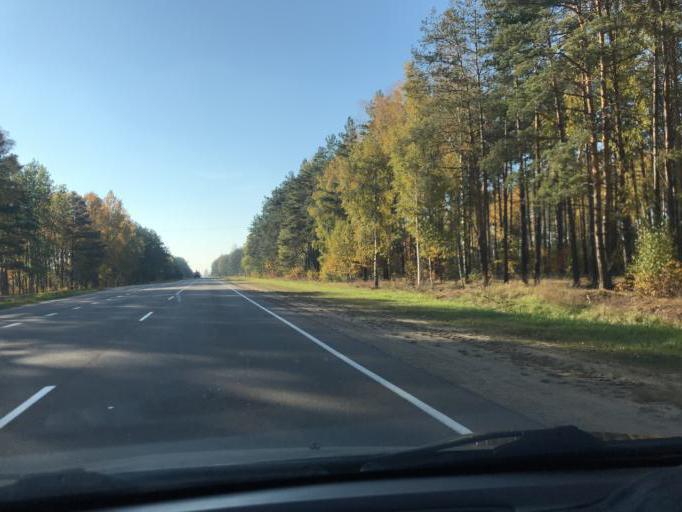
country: BY
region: Minsk
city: Staryya Darohi
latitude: 53.0452
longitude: 28.3491
